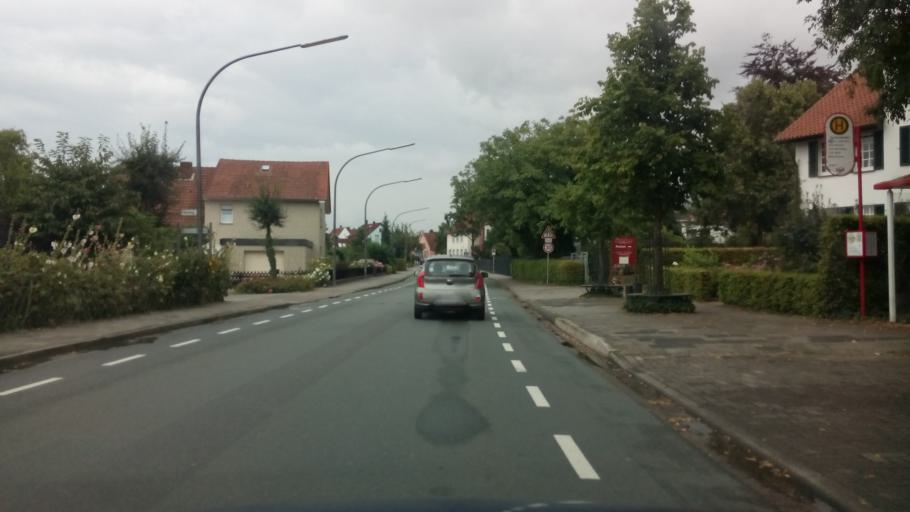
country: DE
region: Lower Saxony
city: Bad Essen
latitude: 52.3210
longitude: 8.3415
